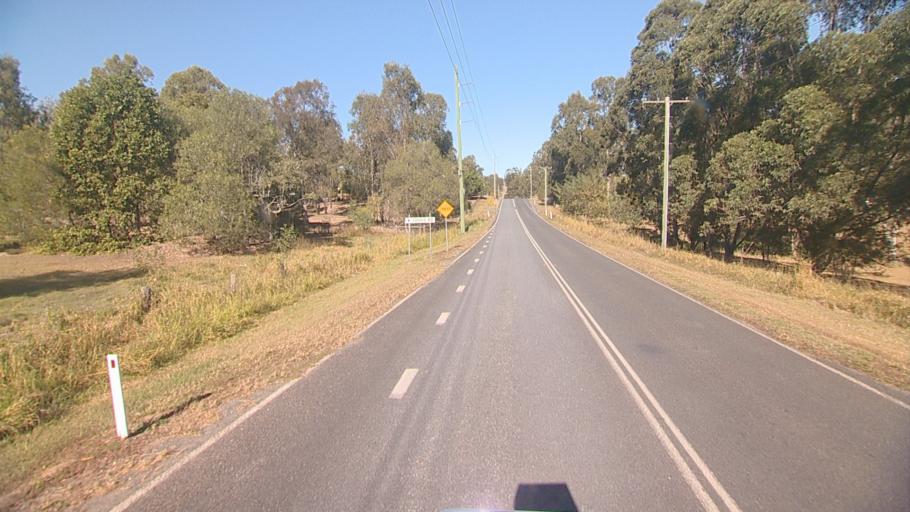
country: AU
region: Queensland
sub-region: Logan
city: Cedar Vale
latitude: -27.8684
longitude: 153.0180
